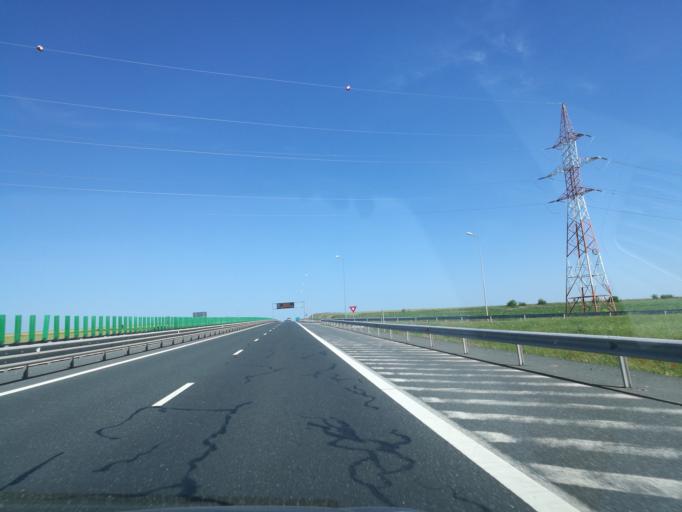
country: RO
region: Constanta
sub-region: Oras Murfatlar
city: Siminoc
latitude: 44.1532
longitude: 28.3532
